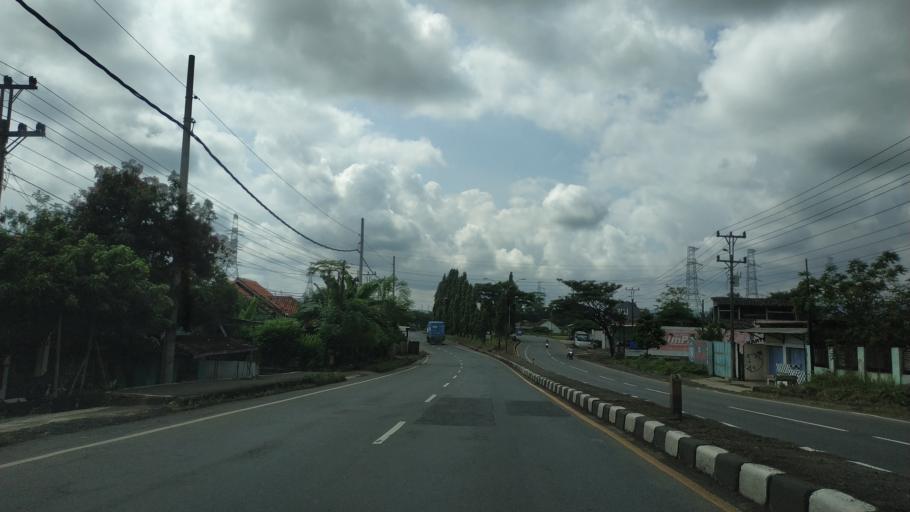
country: ID
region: Central Java
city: Pekalongan
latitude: -6.9499
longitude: 109.7904
